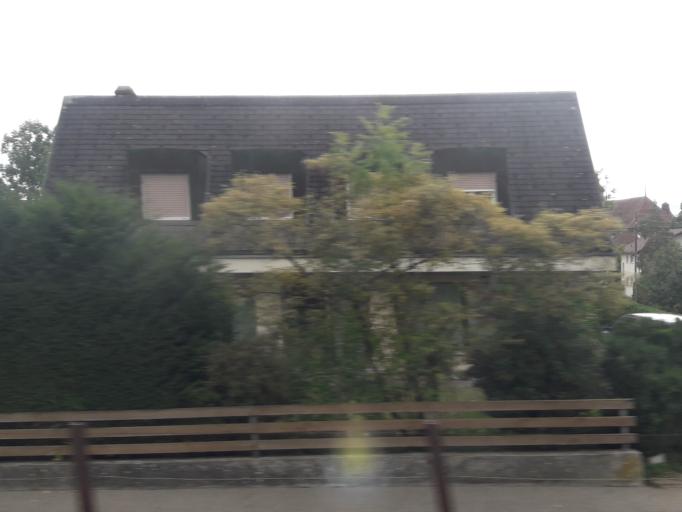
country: CH
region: Bern
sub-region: Bern-Mittelland District
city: Belp
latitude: 46.8912
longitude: 7.4969
